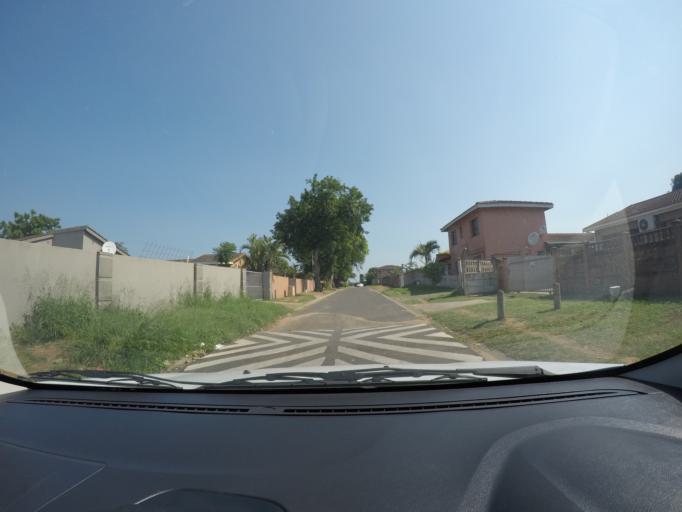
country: ZA
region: KwaZulu-Natal
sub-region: uThungulu District Municipality
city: Richards Bay
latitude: -28.7233
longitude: 32.0449
